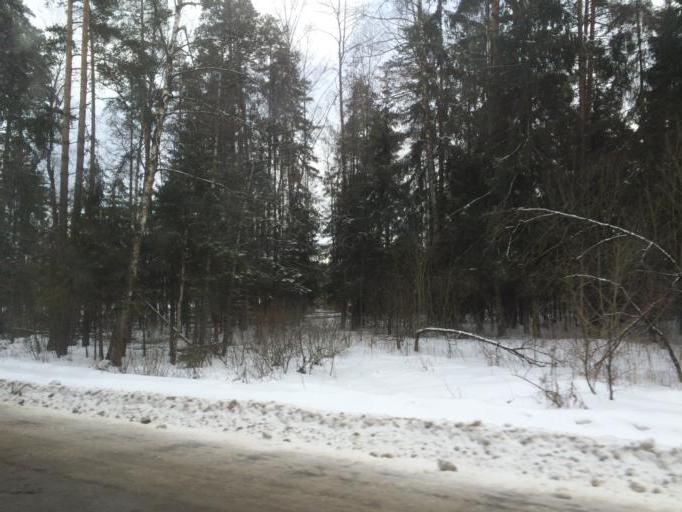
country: RU
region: Moskovskaya
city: Pavlovskaya Sloboda
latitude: 55.7975
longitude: 37.1388
